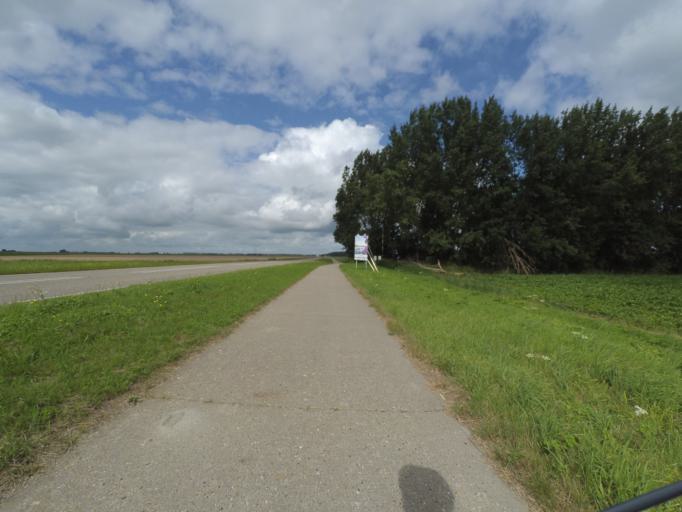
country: NL
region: Groningen
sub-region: Gemeente Zuidhorn
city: Grijpskerk
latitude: 53.3161
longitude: 6.2601
